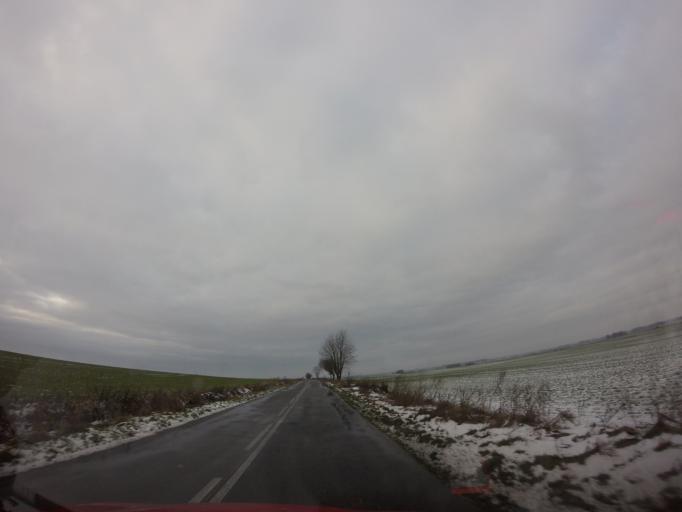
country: PL
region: West Pomeranian Voivodeship
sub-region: Powiat choszczenski
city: Pelczyce
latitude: 53.0531
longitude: 15.3684
